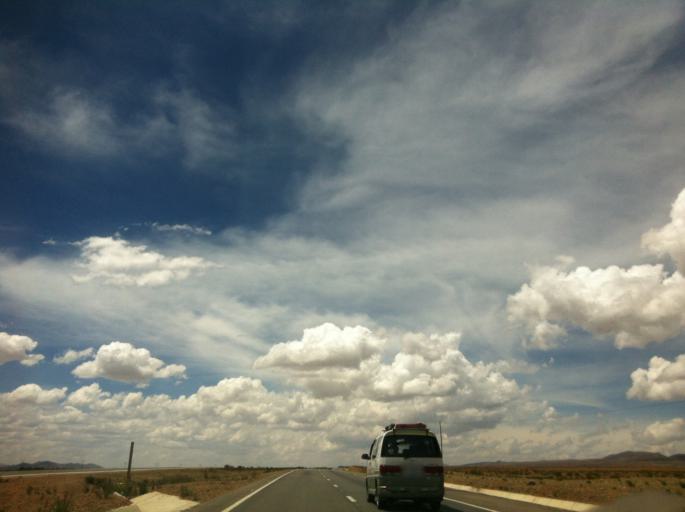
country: BO
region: La Paz
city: Patacamaya
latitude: -17.0853
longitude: -68.0139
